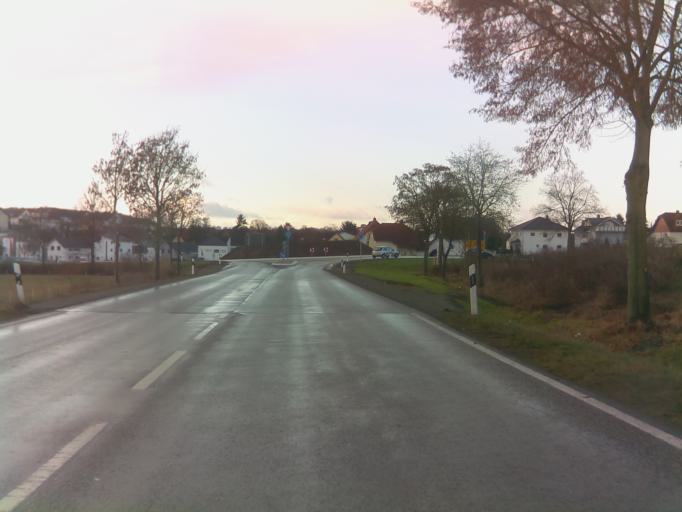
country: DE
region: Hesse
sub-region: Regierungsbezirk Giessen
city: Lich
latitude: 50.5420
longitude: 8.7550
